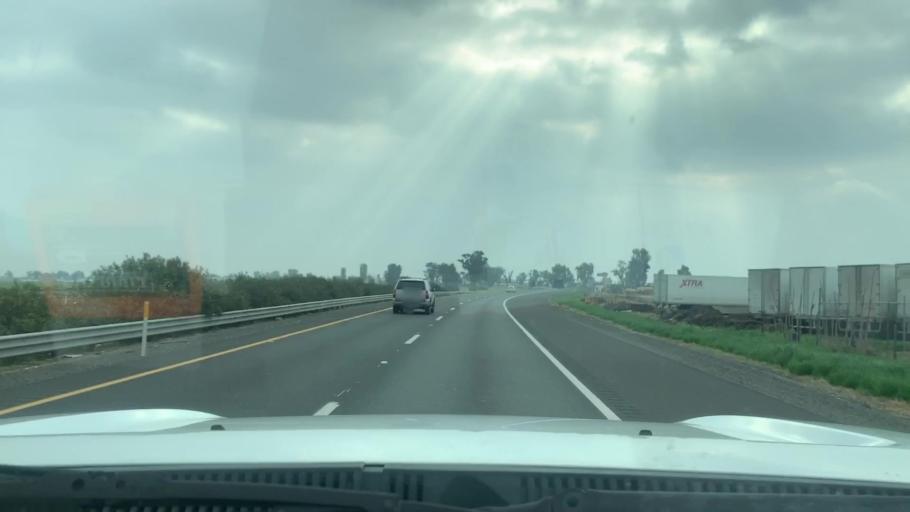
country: US
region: California
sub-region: Tulare County
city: Tulare
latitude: 36.1646
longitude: -119.3319
